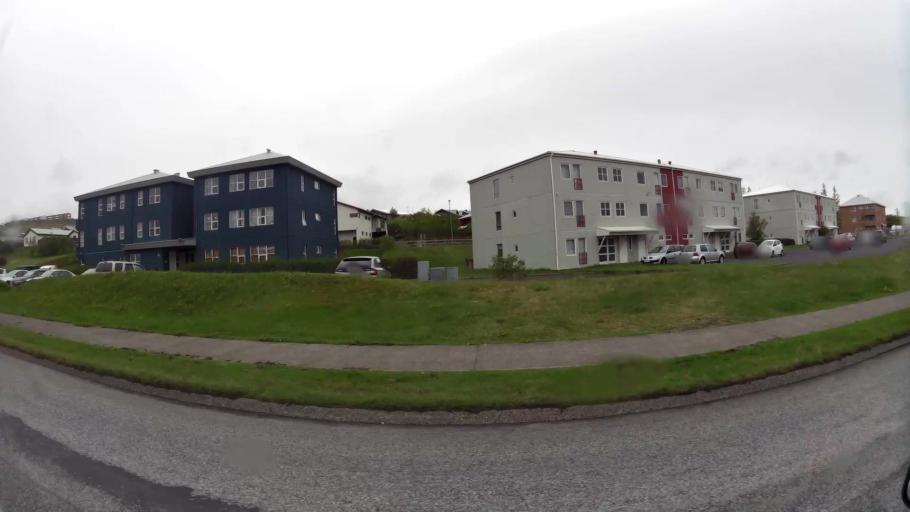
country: IS
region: Capital Region
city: Hafnarfjoerdur
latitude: 64.0623
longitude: -21.9343
